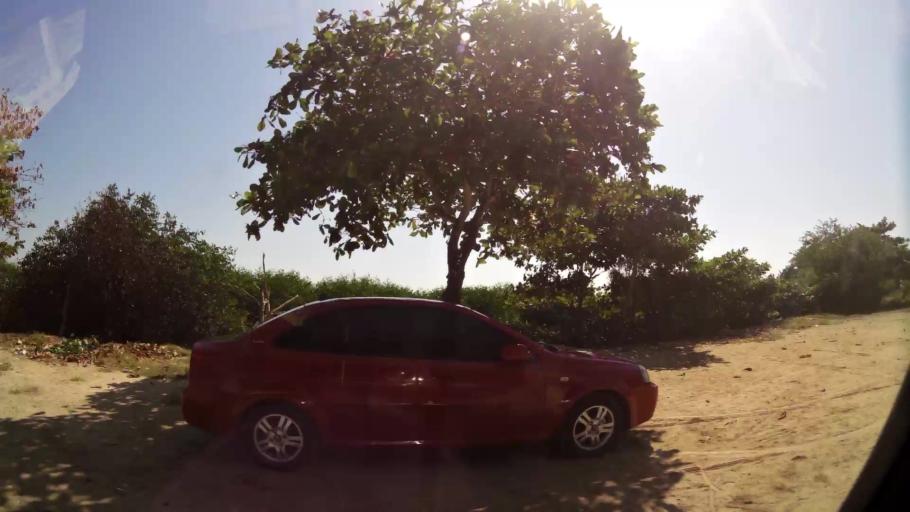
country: CO
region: Bolivar
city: Cartagena
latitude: 10.4374
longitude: -75.5141
